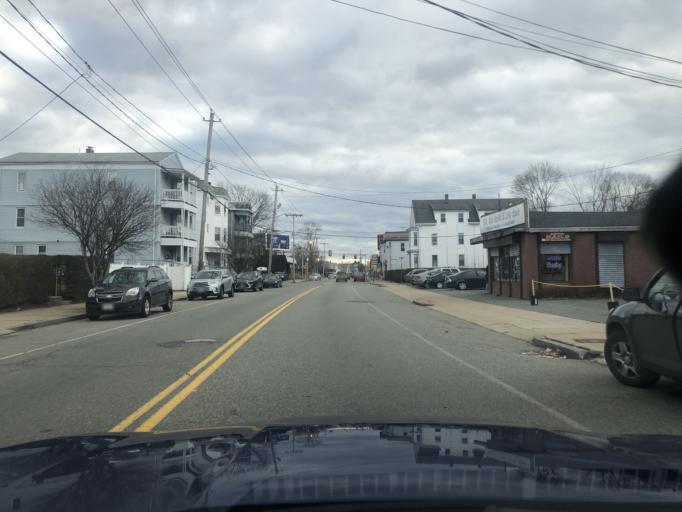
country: US
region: Massachusetts
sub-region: Plymouth County
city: Brockton
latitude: 42.0984
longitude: -71.0199
